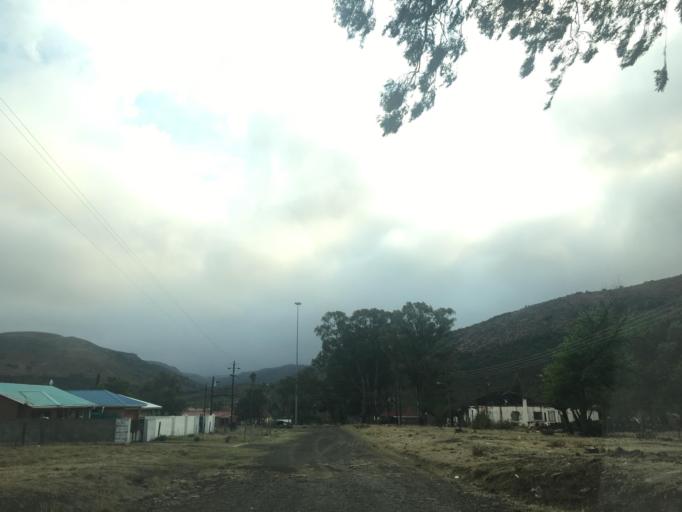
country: ZA
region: Eastern Cape
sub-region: Chris Hani District Municipality
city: Cala
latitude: -31.5233
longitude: 27.6993
